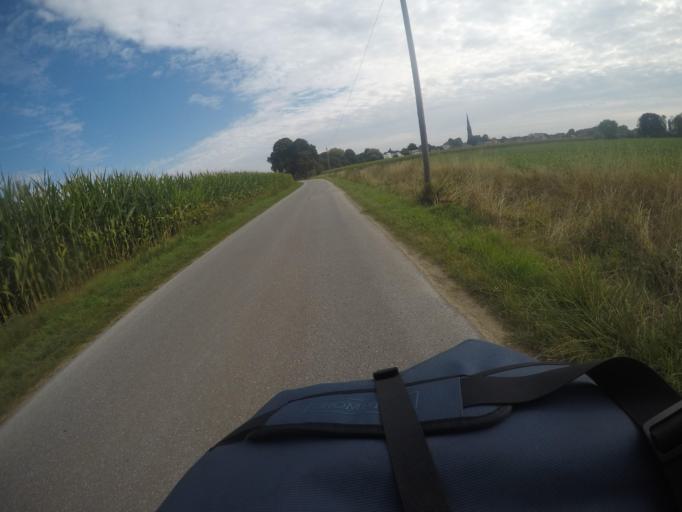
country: DE
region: North Rhine-Westphalia
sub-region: Regierungsbezirk Dusseldorf
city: Emmerich
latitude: 51.8476
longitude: 6.1956
